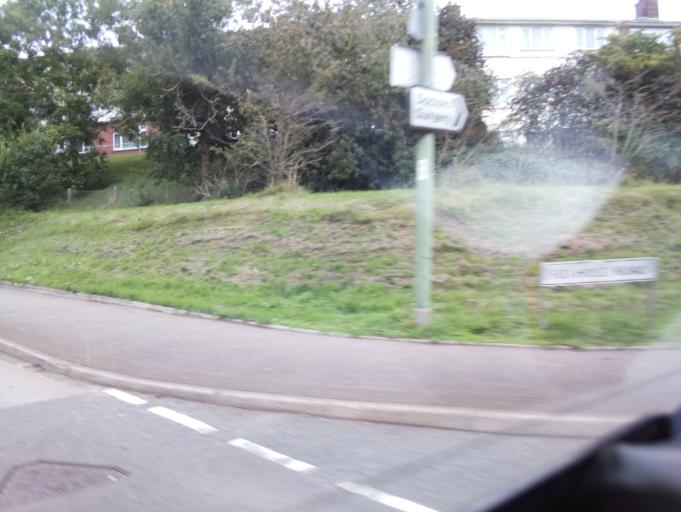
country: GB
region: England
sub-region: Borough of Torbay
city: Paignton
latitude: 50.4356
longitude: -3.5875
